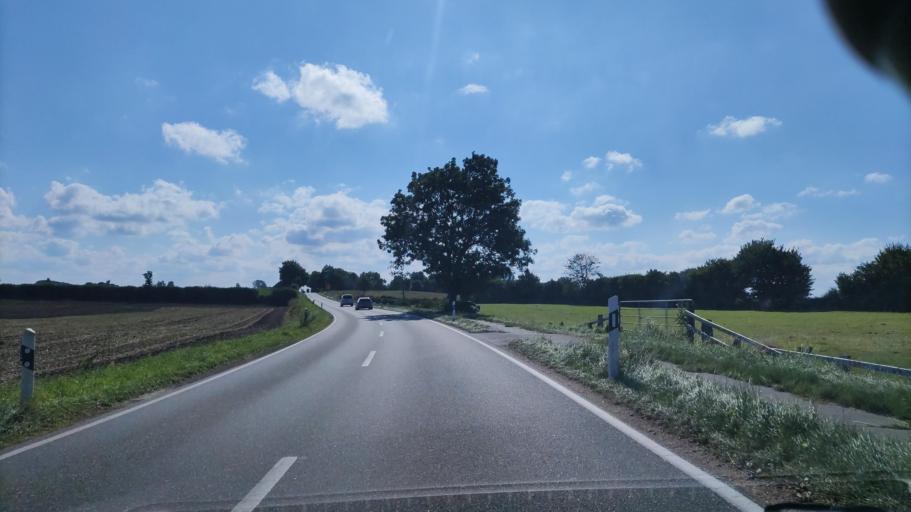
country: DE
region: Schleswig-Holstein
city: Osterby
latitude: 54.4426
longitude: 9.7378
